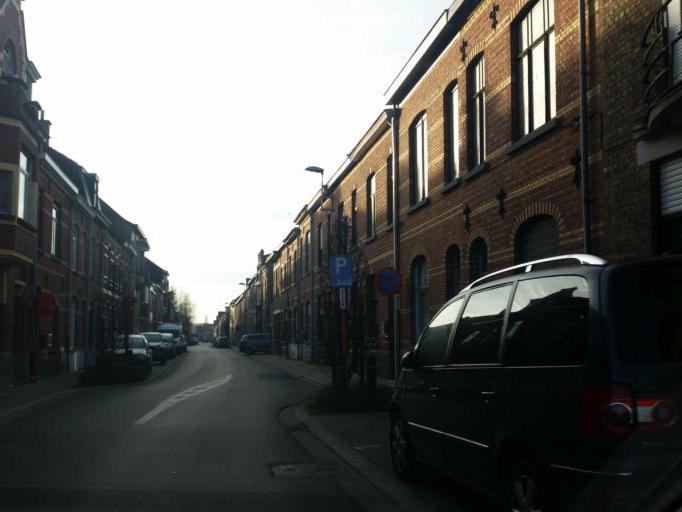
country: BE
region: Flanders
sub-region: Provincie Oost-Vlaanderen
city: Eeklo
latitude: 51.1794
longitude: 3.5728
